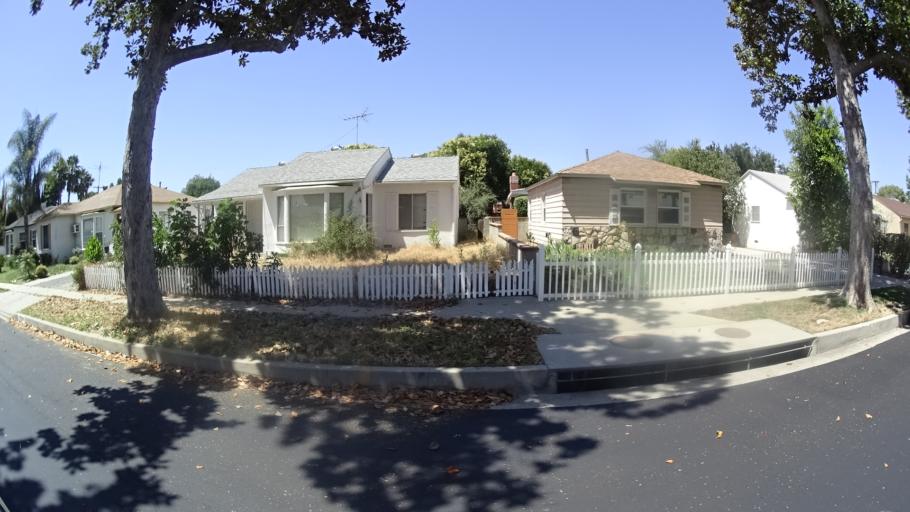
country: US
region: California
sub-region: Los Angeles County
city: Northridge
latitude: 34.1885
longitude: -118.5165
